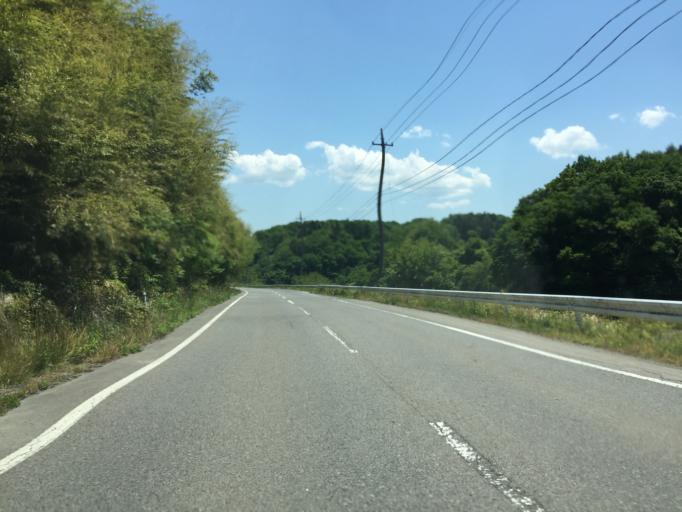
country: JP
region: Fukushima
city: Funehikimachi-funehiki
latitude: 37.4809
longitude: 140.5662
